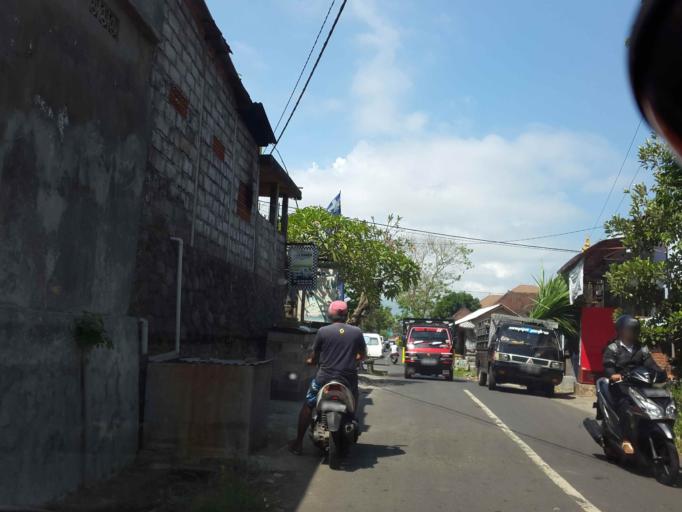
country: ID
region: Bali
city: Klungkung
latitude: -8.5448
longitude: 115.3656
